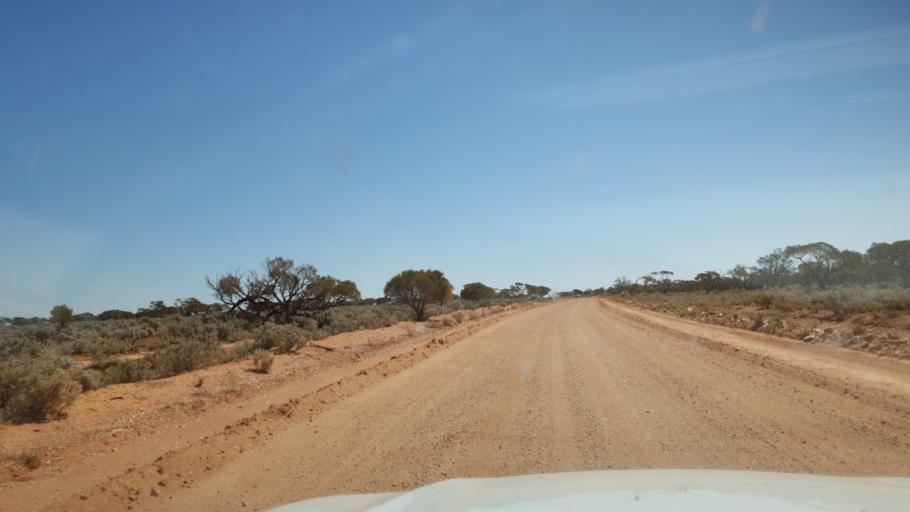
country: AU
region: South Australia
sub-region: Whyalla
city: Whyalla
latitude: -32.6336
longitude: 136.8510
